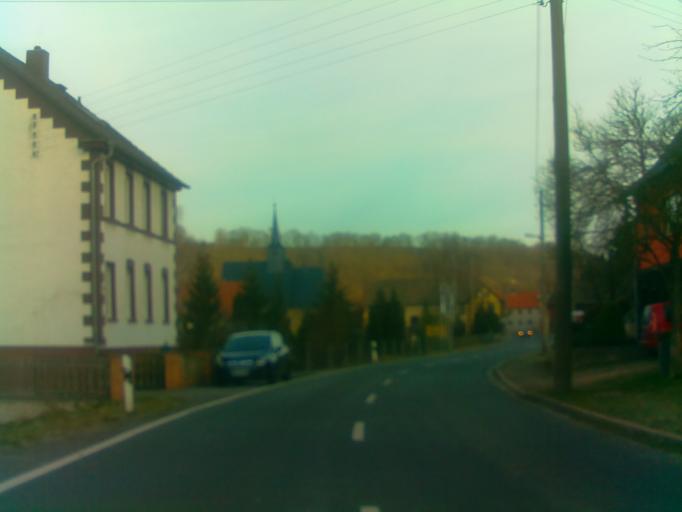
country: DE
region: Thuringia
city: Freienorla
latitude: 50.7673
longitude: 11.5425
